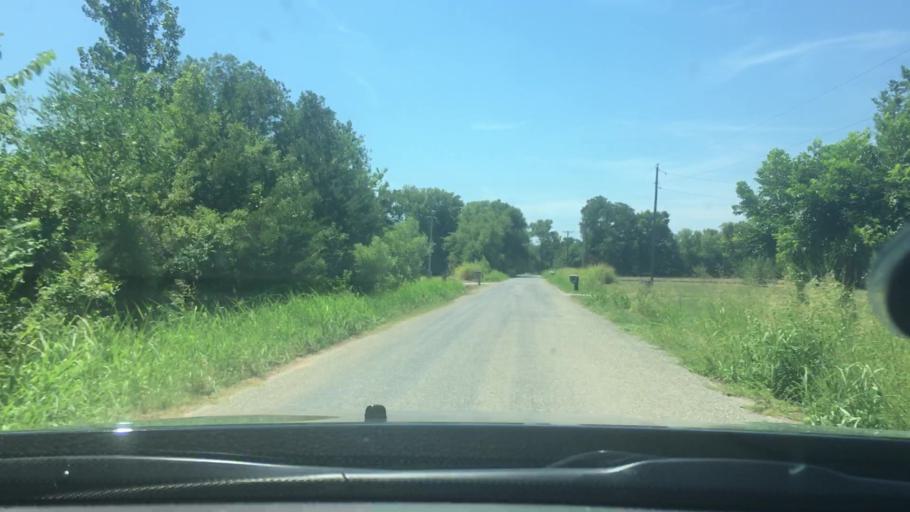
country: US
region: Oklahoma
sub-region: Bryan County
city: Durant
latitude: 33.9921
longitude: -96.2684
